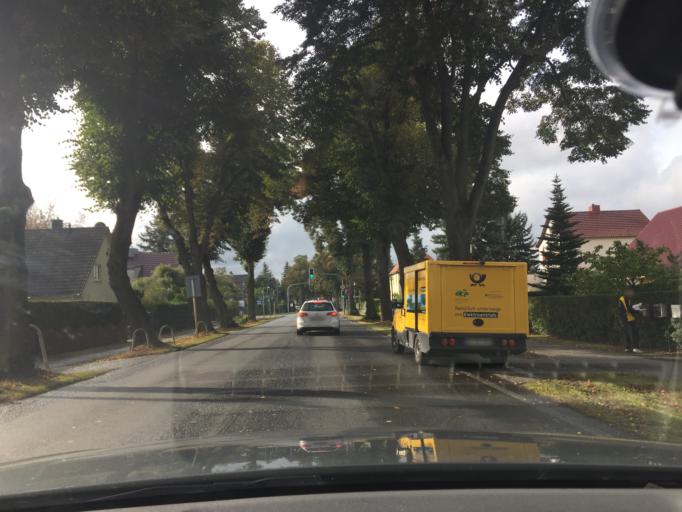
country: DE
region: Berlin
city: Hellersdorf
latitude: 52.5354
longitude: 13.6322
